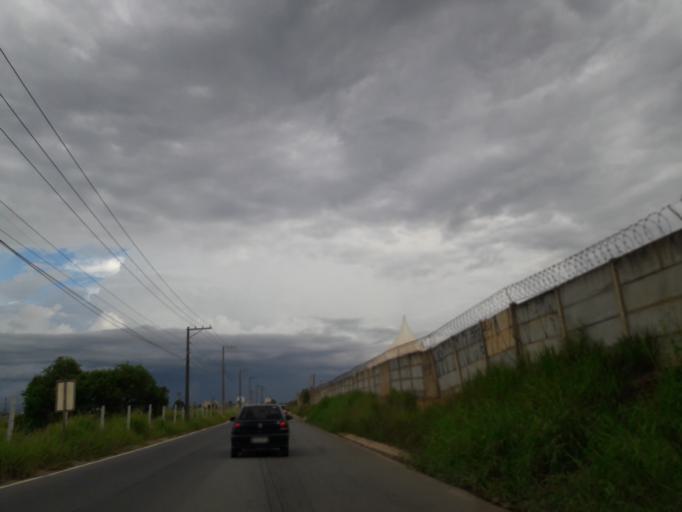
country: BR
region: Sao Paulo
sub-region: Aruja
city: Aruja
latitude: -23.3928
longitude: -46.4097
